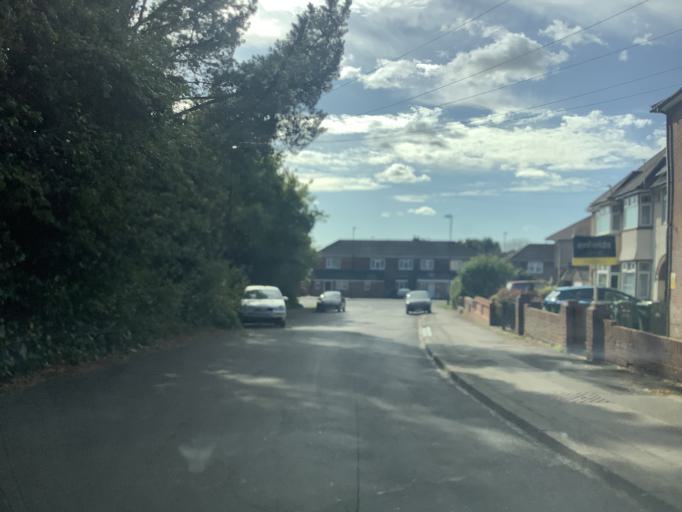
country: GB
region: England
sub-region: Hampshire
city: Marchwood
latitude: 50.9234
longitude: -1.4494
